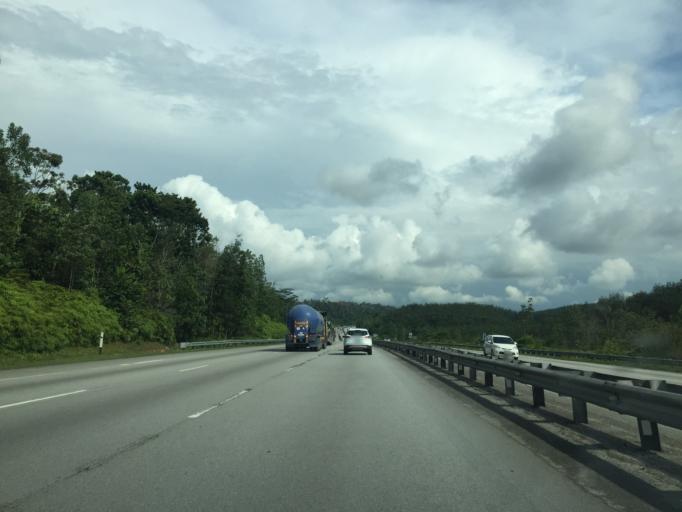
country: MY
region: Selangor
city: Batang Berjuntai
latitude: 3.5447
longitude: 101.5185
